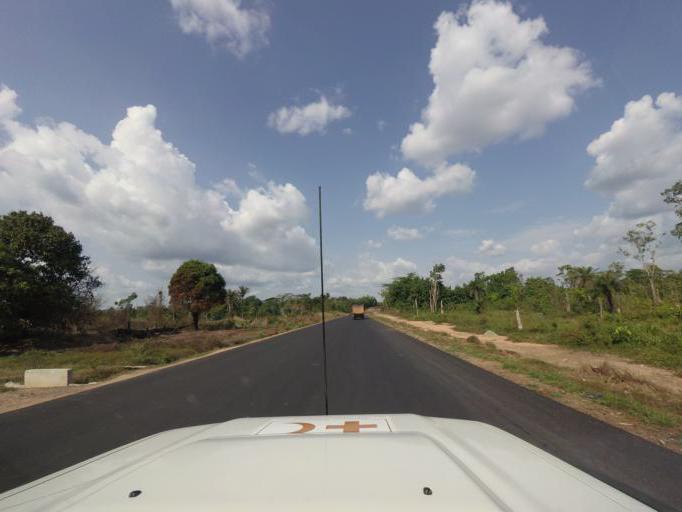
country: LR
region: Bong
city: Gbarnga
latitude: 6.9857
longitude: -9.5951
